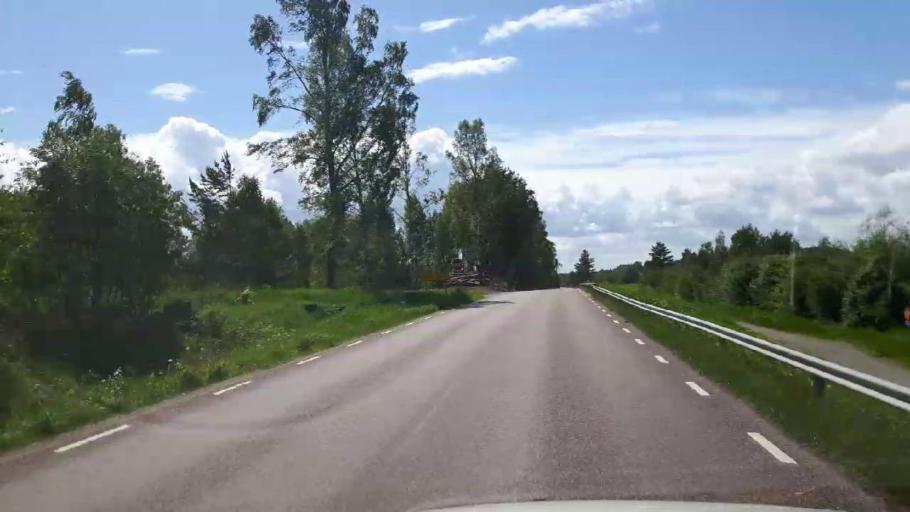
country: SE
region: Dalarna
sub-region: Faluns Kommun
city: Falun
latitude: 60.6101
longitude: 15.7728
